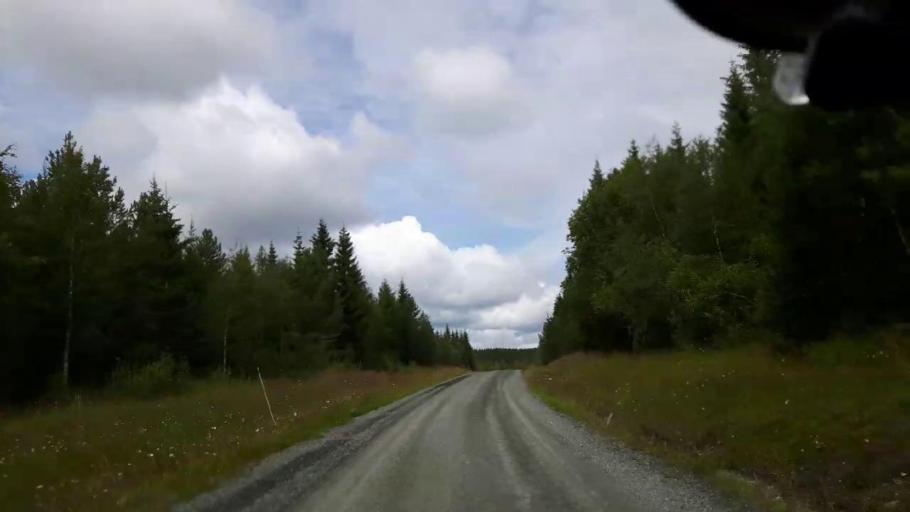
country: SE
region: Jaemtland
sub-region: Krokoms Kommun
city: Valla
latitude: 63.5604
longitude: 13.9158
